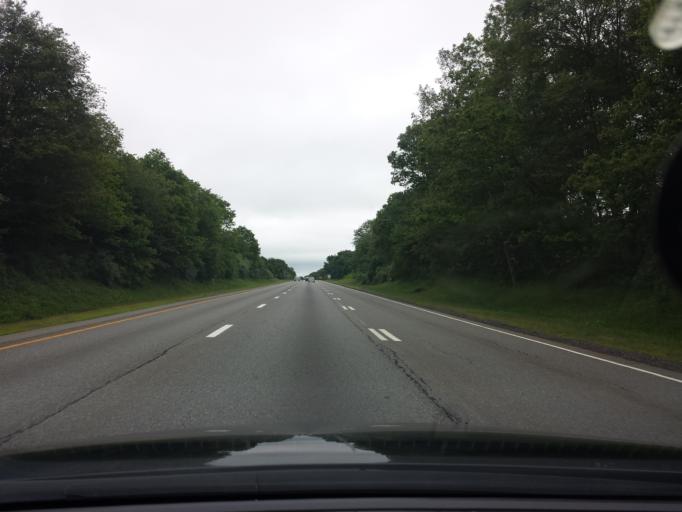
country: US
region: Connecticut
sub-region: New London County
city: Old Mystic
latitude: 41.3735
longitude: -71.9453
